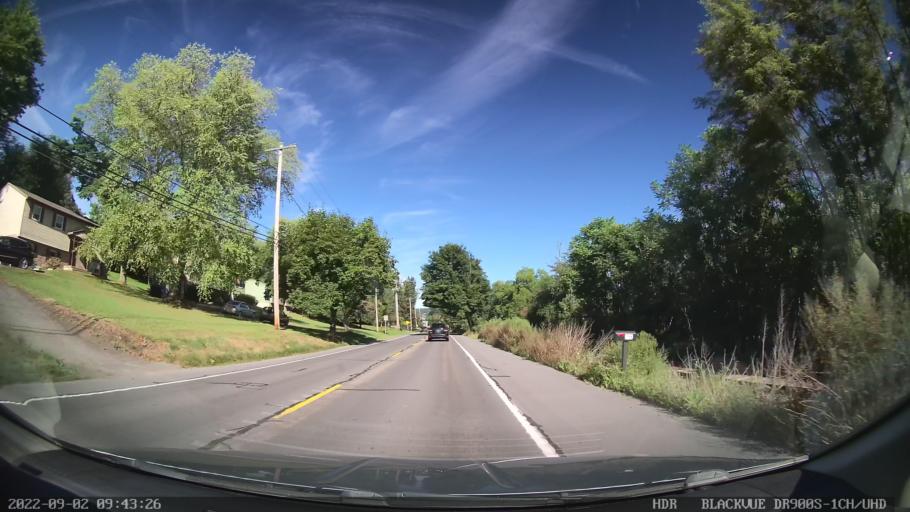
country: US
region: Pennsylvania
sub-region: Northumberland County
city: Riverside
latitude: 40.9533
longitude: -76.6198
